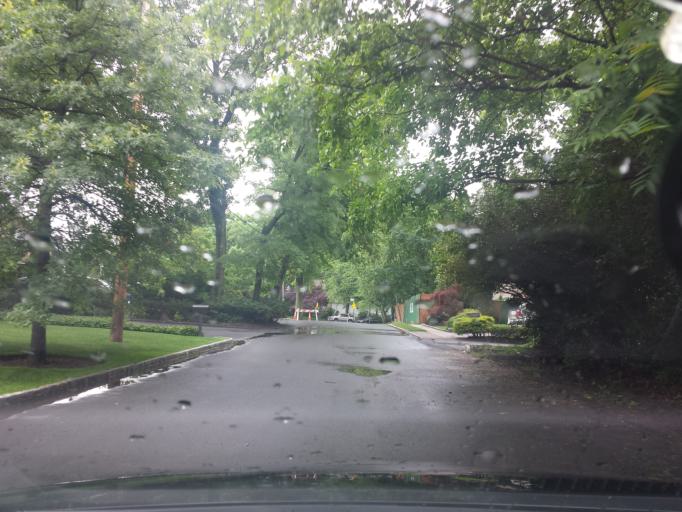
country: US
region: New York
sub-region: Richmond County
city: Staten Island
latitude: 40.5833
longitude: -74.1260
